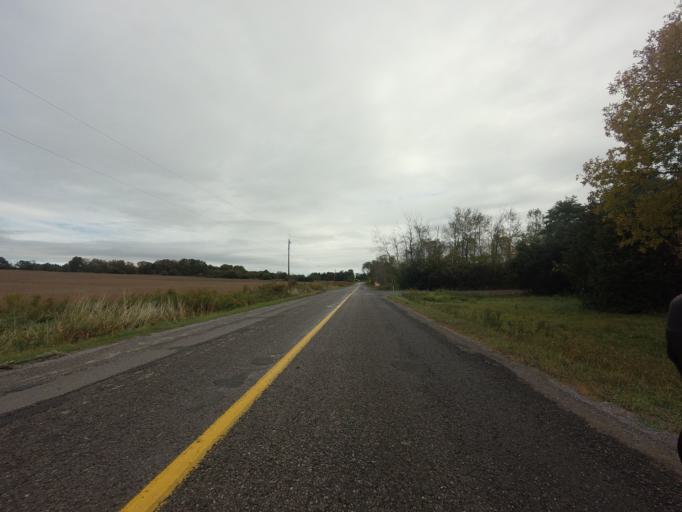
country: CA
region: Ontario
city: Cobourg
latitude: 43.9058
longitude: -78.5022
